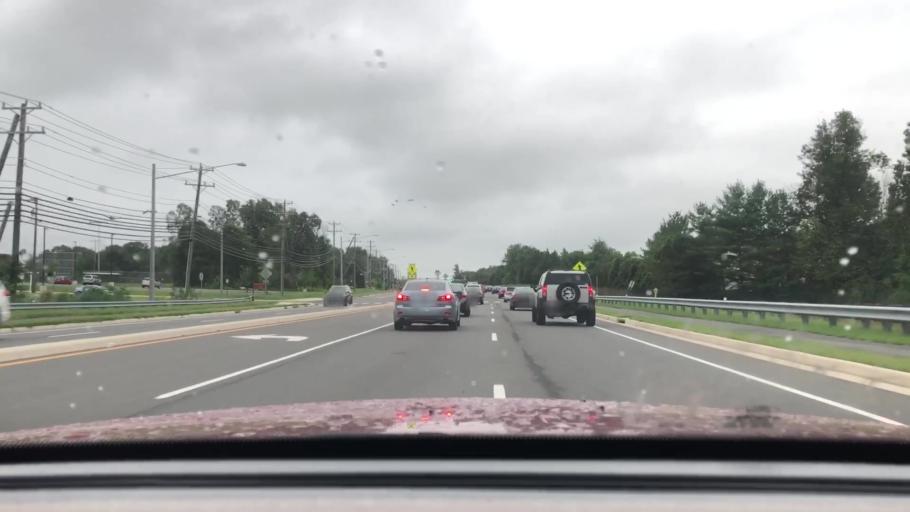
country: US
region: Virginia
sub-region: Fairfax County
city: Greenbriar
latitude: 38.8678
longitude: -77.4075
